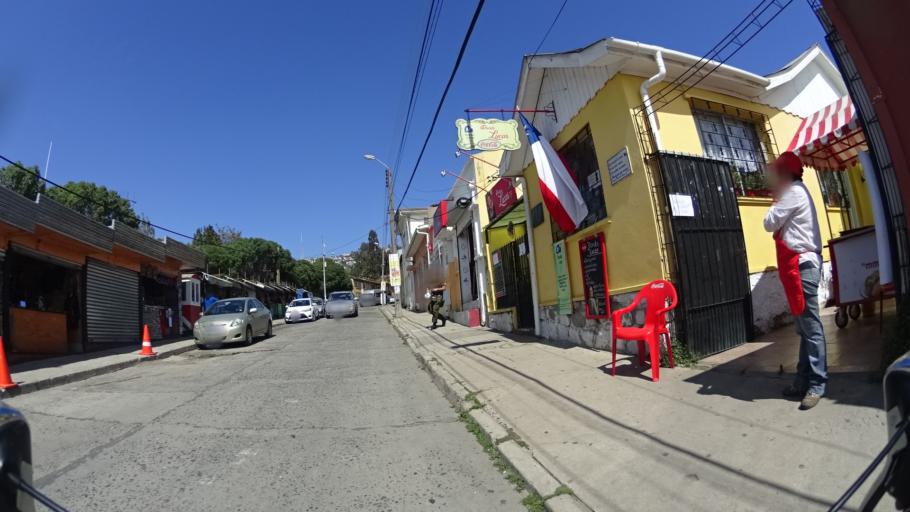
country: CL
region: Valparaiso
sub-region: Provincia de Valparaiso
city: Valparaiso
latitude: -33.0533
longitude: -71.6223
